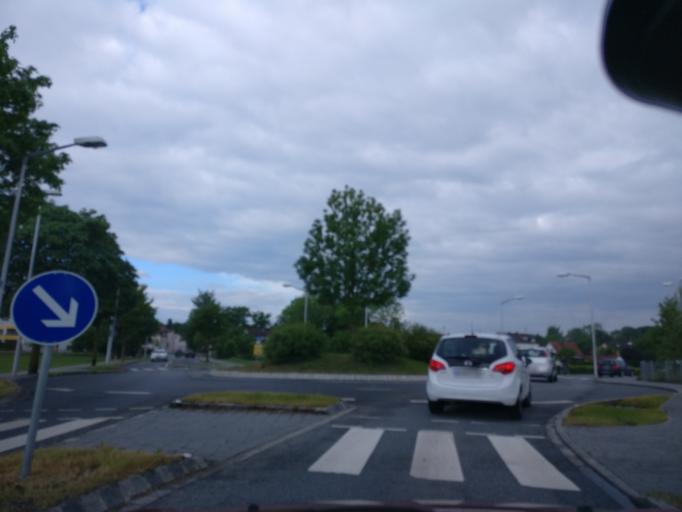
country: DE
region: Bavaria
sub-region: Upper Bavaria
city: Karlsfeld
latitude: 48.2216
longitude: 11.4672
